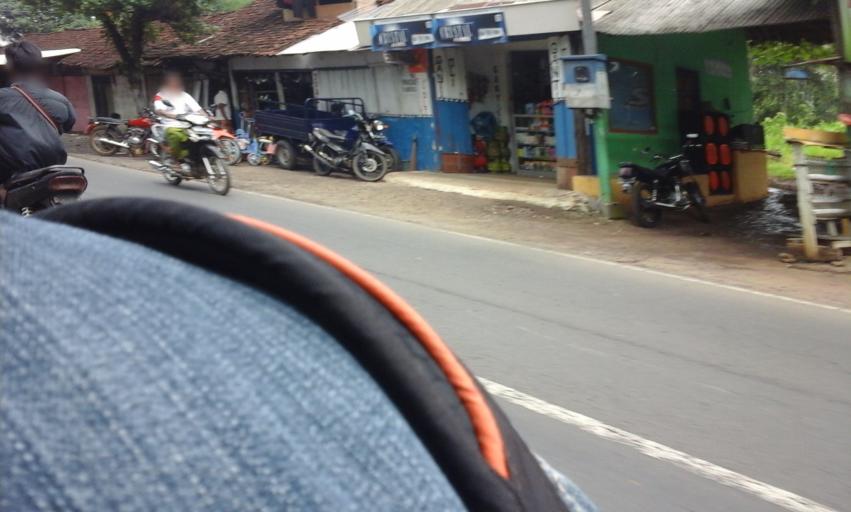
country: ID
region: East Java
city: Klatakan
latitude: -8.1932
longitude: 113.5034
